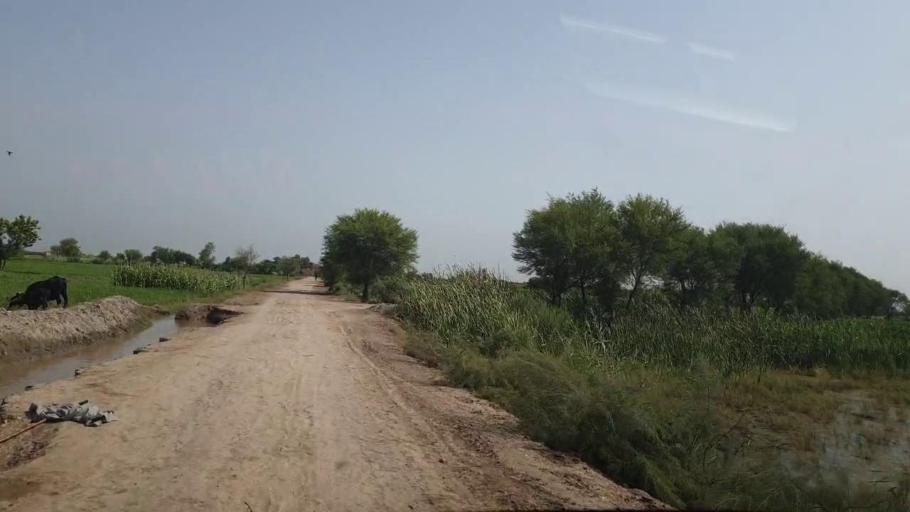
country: PK
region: Sindh
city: Sakrand
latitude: 26.2891
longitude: 68.2265
